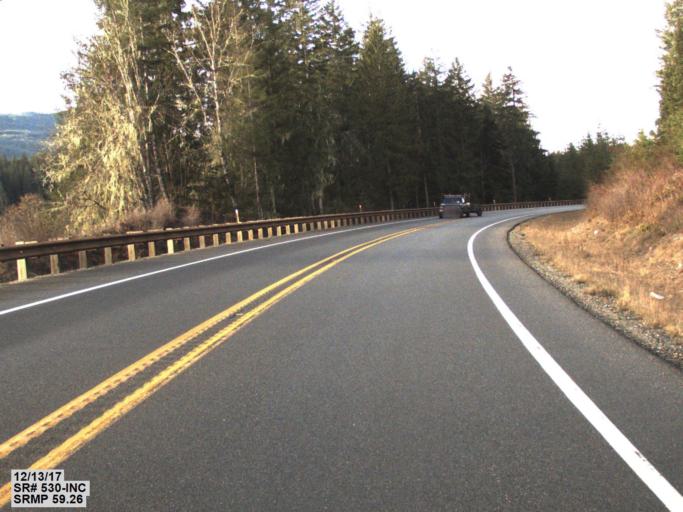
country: US
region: Washington
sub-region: Snohomish County
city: Darrington
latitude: 48.3794
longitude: -121.5540
